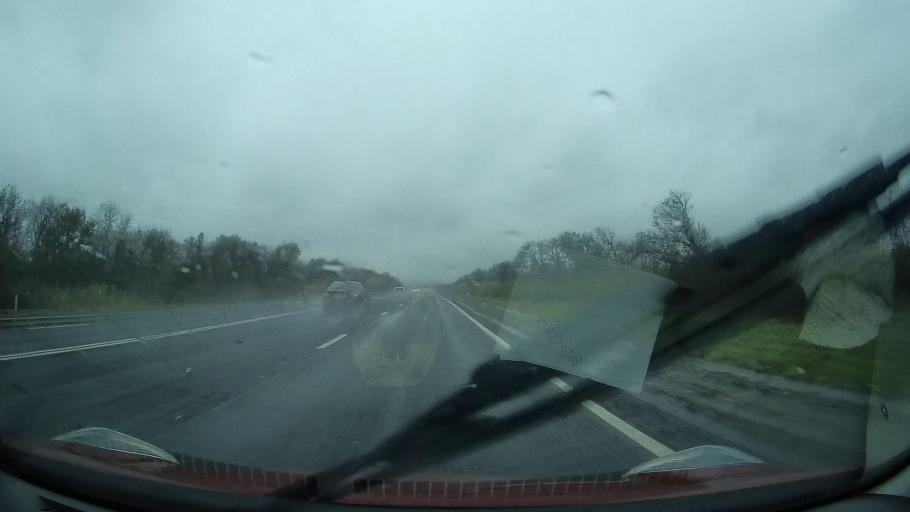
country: RU
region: Stavropol'skiy
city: Nevinnomyssk
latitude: 44.6178
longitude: 42.0995
